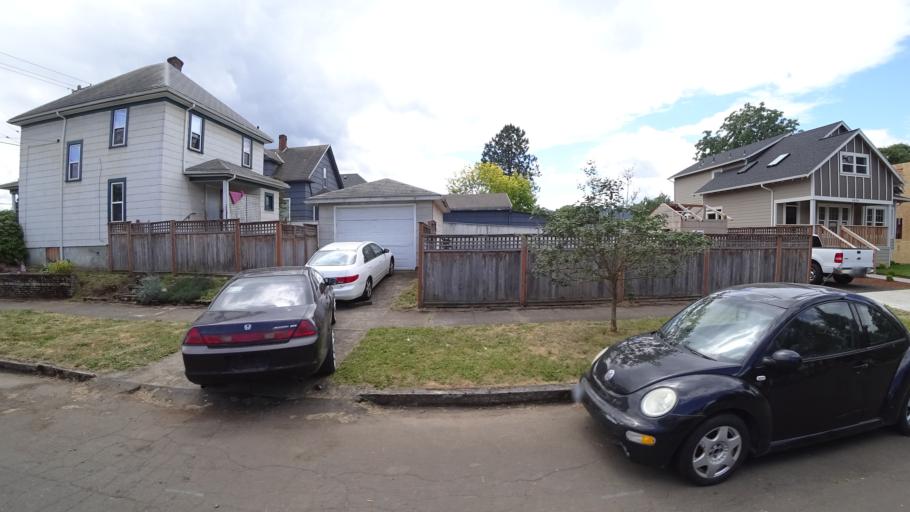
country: US
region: Oregon
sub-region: Washington County
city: West Haven
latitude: 45.5817
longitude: -122.7371
